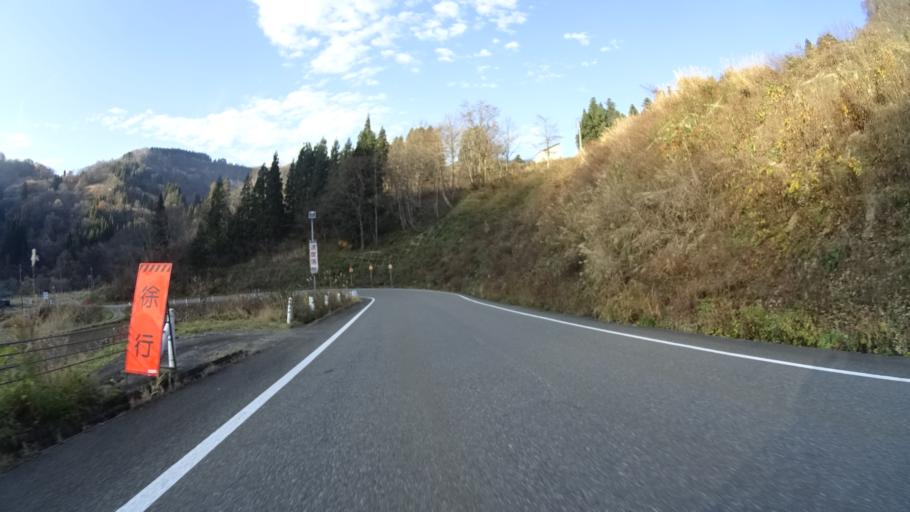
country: JP
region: Niigata
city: Shiozawa
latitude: 36.9892
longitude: 138.7625
